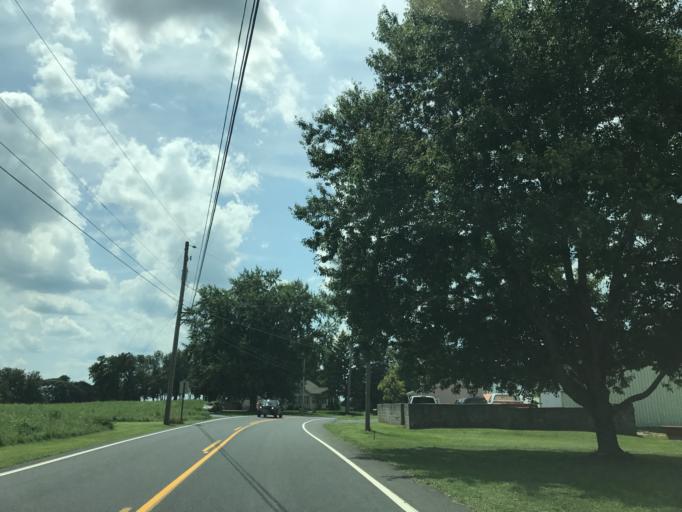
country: US
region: Pennsylvania
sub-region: Lancaster County
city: Manheim
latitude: 40.1807
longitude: -76.4689
